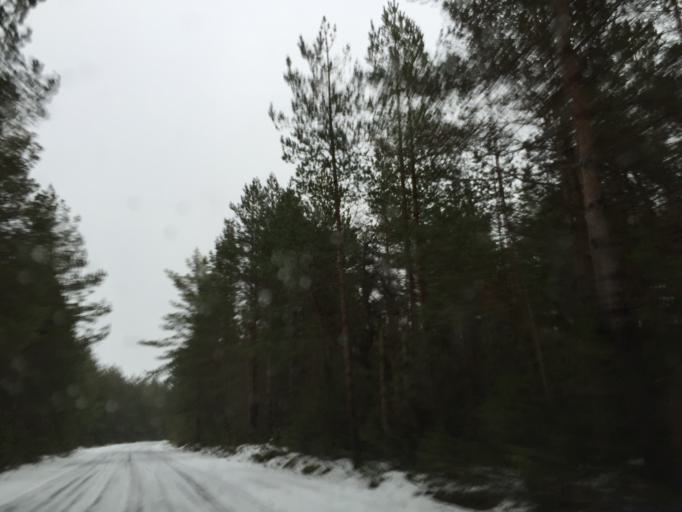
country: EE
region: Laeaene
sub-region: Lihula vald
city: Lihula
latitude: 58.6144
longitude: 23.5585
